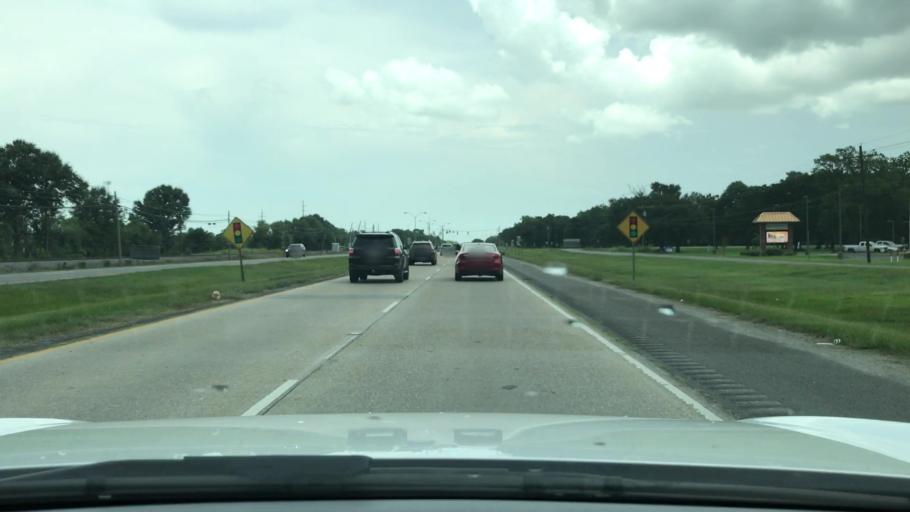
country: US
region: Louisiana
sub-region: Iberville Parish
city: Plaquemine
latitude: 30.3111
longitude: -91.2474
